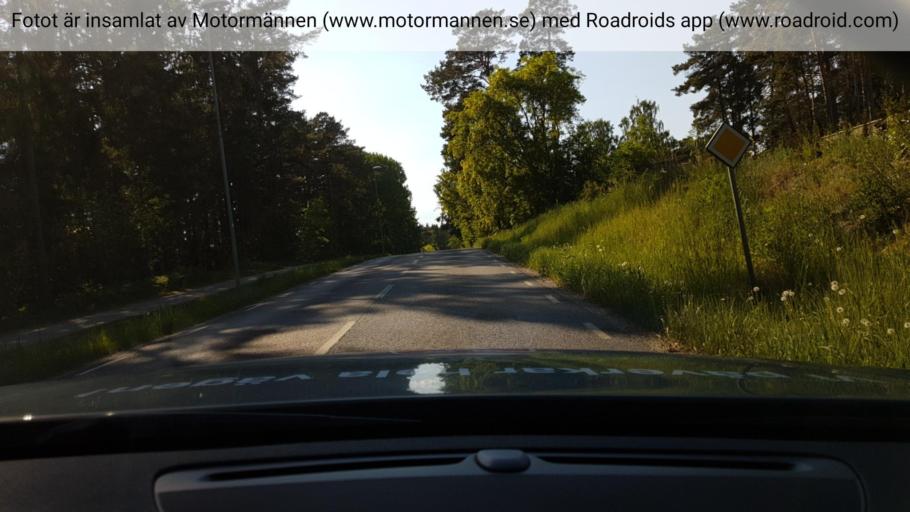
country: SE
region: Stockholm
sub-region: Varmdo Kommun
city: Holo
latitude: 59.2864
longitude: 18.6932
